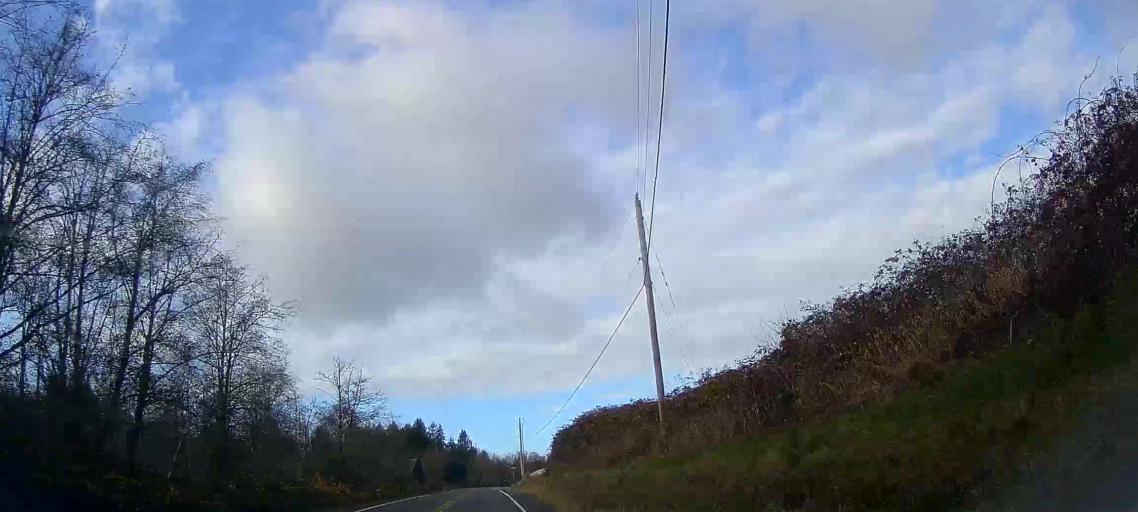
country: US
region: Washington
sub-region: Skagit County
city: Big Lake
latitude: 48.4105
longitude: -122.2196
